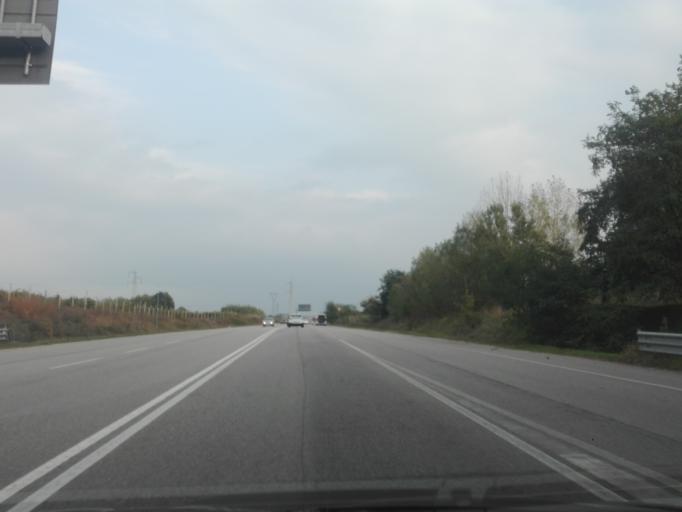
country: IT
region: Veneto
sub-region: Provincia di Verona
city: Bussolengo
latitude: 45.4564
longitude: 10.8512
